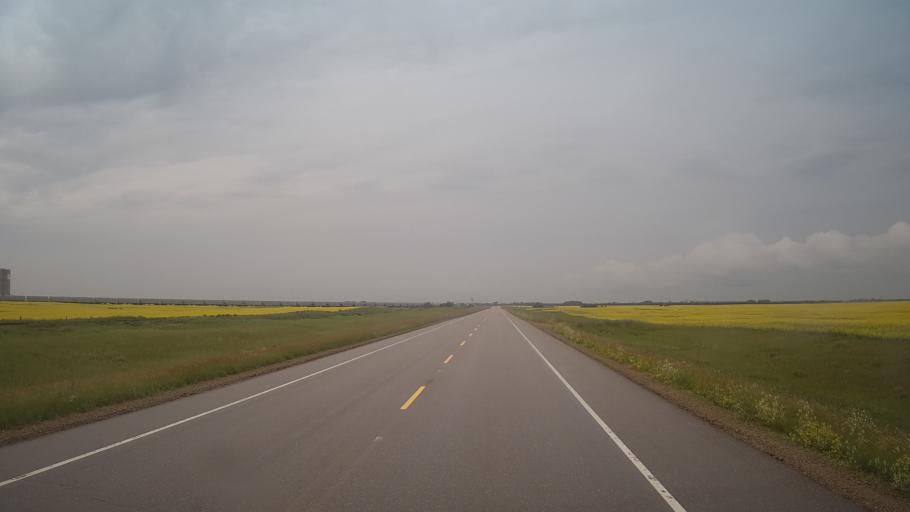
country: CA
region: Saskatchewan
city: Wilkie
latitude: 52.3005
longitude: -108.6733
